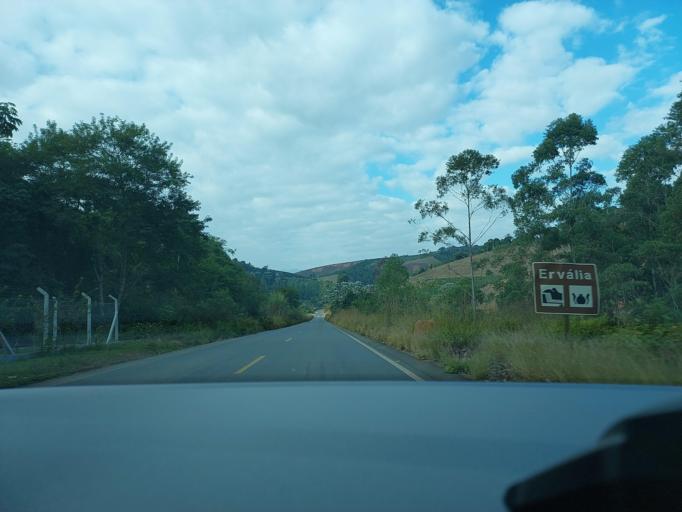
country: BR
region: Minas Gerais
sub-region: Vicosa
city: Vicosa
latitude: -20.8381
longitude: -42.6983
